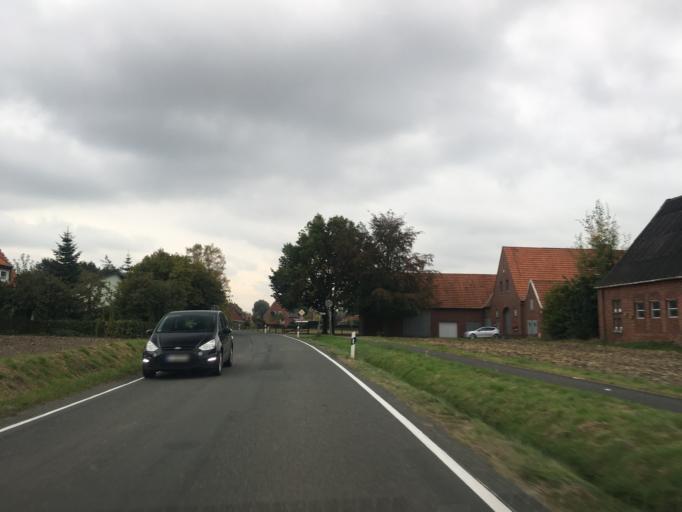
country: DE
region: North Rhine-Westphalia
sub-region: Regierungsbezirk Munster
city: Nordwalde
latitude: 52.1037
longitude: 7.4669
